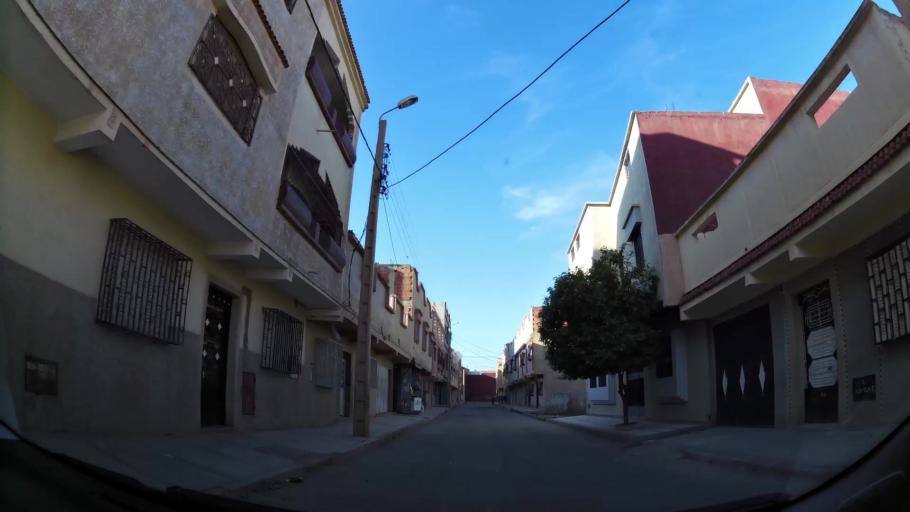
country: MA
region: Oriental
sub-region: Oujda-Angad
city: Oujda
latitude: 34.7063
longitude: -1.8951
